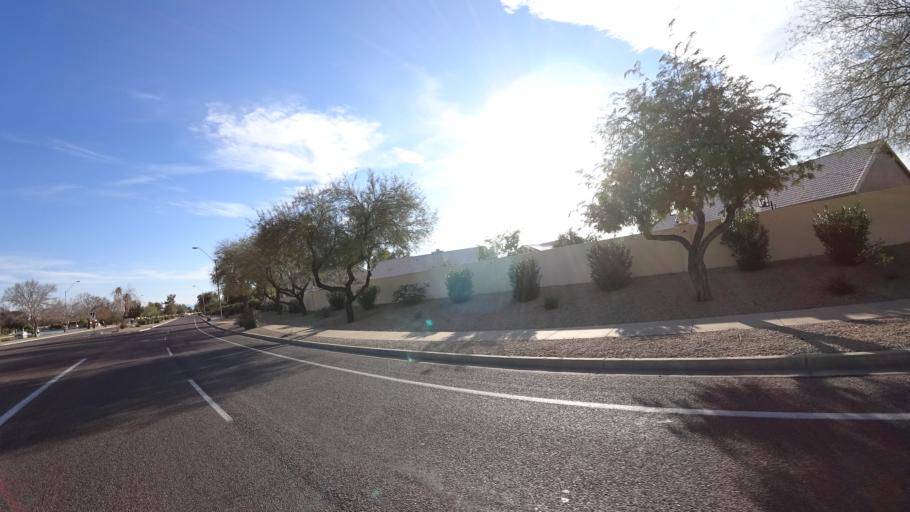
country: US
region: Arizona
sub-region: Maricopa County
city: Sun City
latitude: 33.6167
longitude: -112.2537
